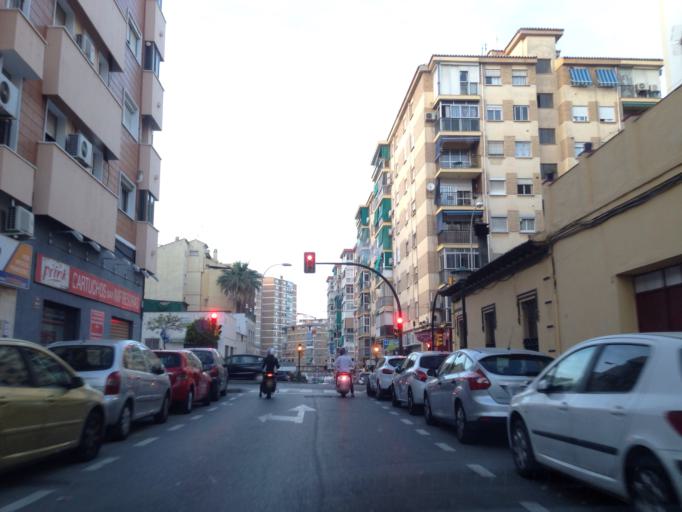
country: ES
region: Andalusia
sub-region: Provincia de Malaga
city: Malaga
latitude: 36.7285
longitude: -4.4427
